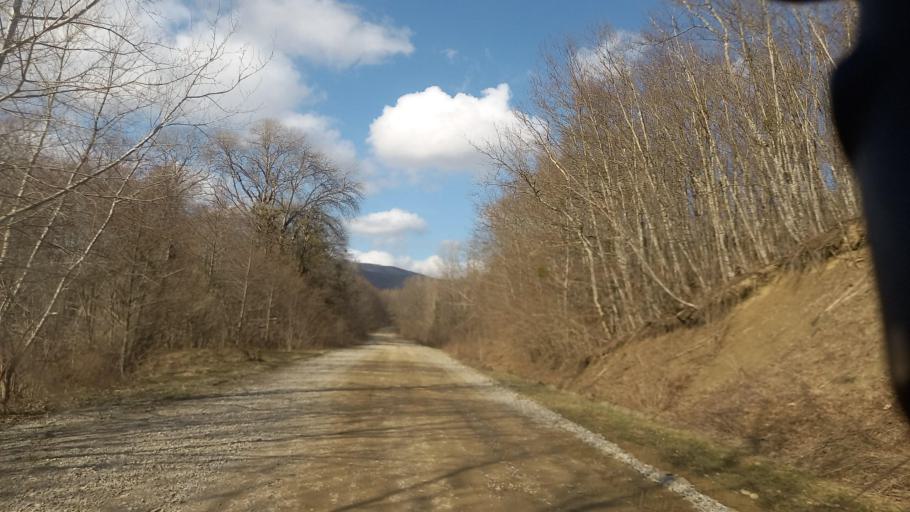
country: RU
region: Krasnodarskiy
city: Smolenskaya
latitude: 44.6090
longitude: 38.8368
